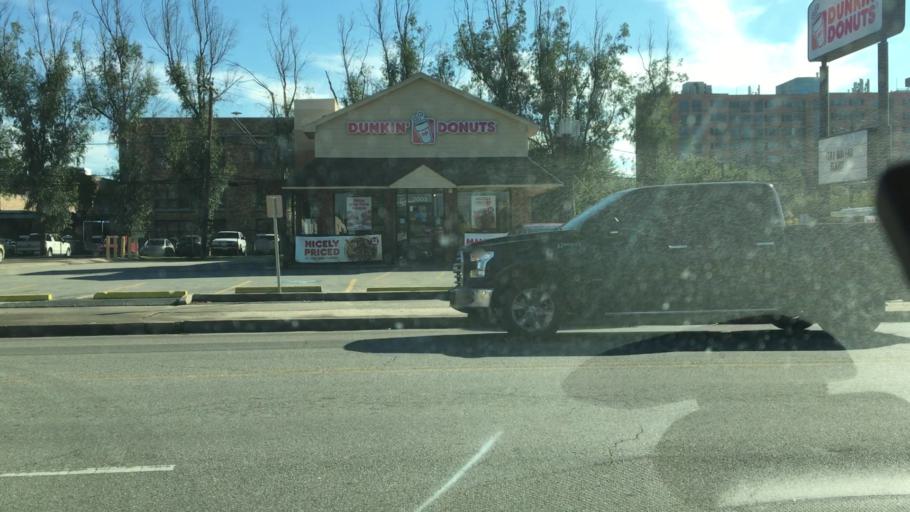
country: US
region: Texas
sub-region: Harris County
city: Houston
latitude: 29.8043
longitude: -95.3993
